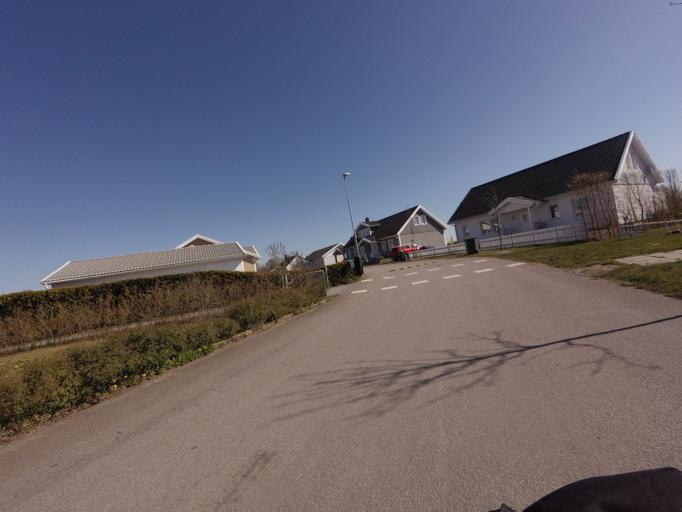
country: SE
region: Skane
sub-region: Malmo
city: Oxie
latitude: 55.4632
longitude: 13.1394
